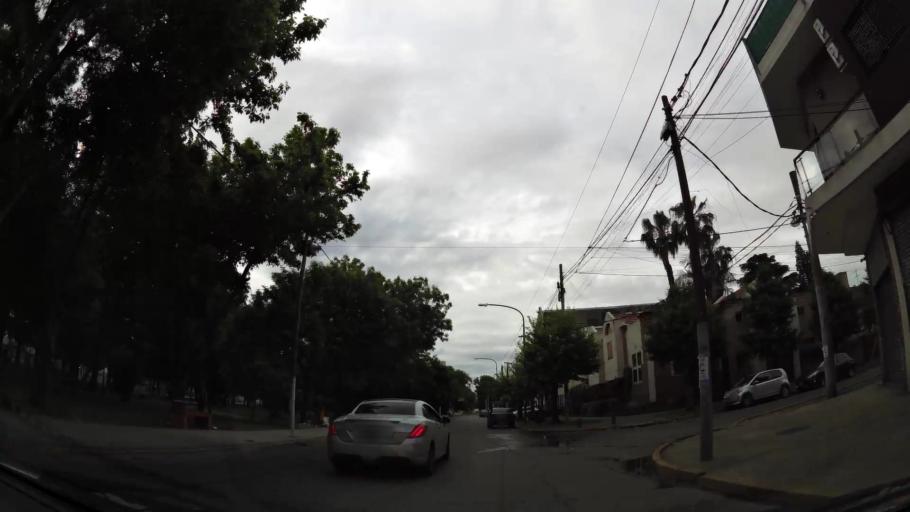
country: AR
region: Buenos Aires
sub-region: Partido de Quilmes
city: Quilmes
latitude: -34.7317
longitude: -58.2541
